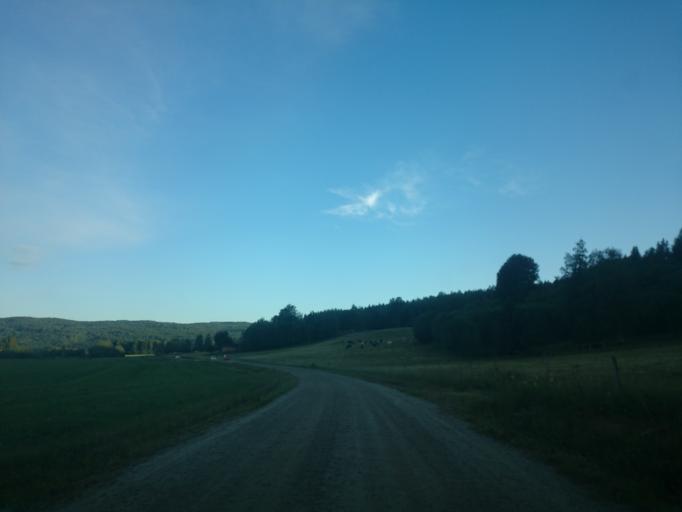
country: SE
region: Vaesternorrland
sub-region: Kramfors Kommun
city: Bollstabruk
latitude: 63.0643
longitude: 17.7337
